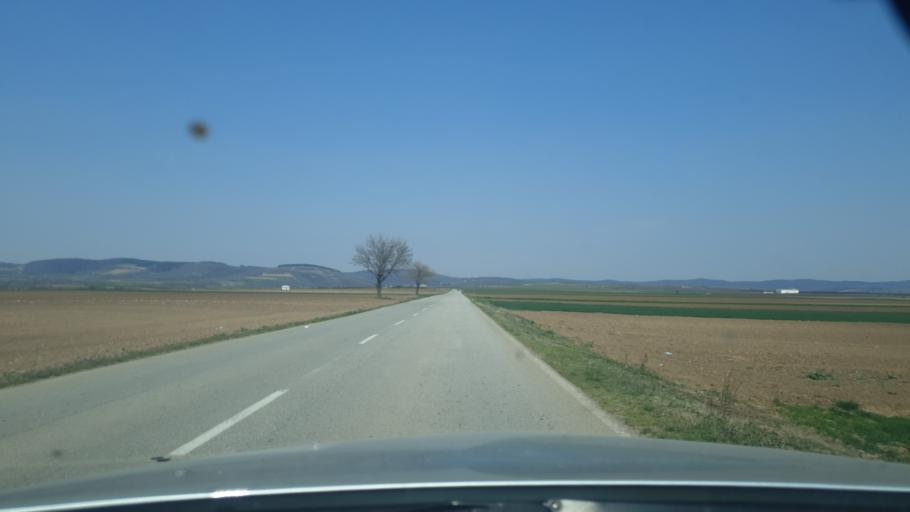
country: RS
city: Vrdnik
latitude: 45.0764
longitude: 19.7698
